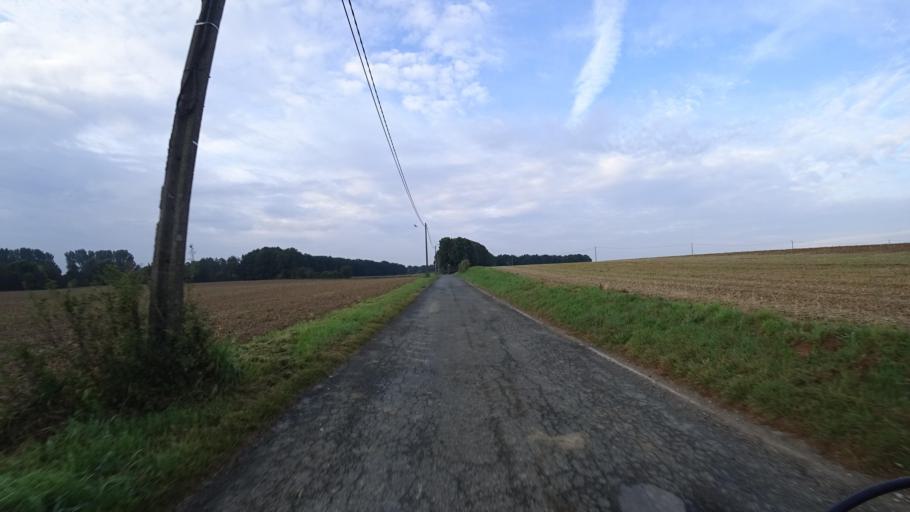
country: BE
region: Wallonia
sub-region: Province du Brabant Wallon
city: Walhain-Saint-Paul
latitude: 50.5984
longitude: 4.7553
